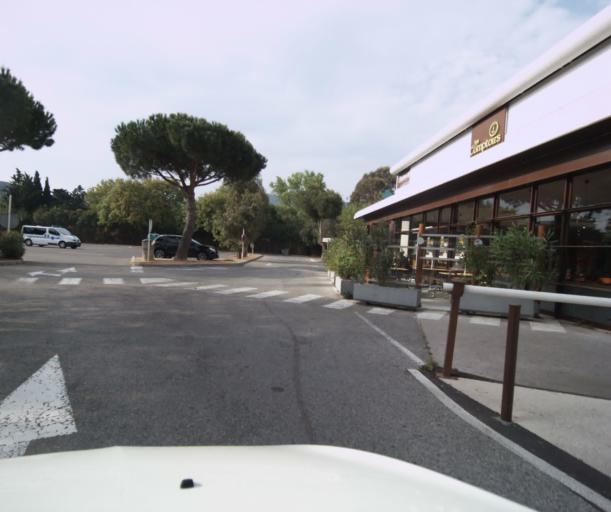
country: FR
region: Provence-Alpes-Cote d'Azur
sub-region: Departement du Var
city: Hyeres
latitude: 43.1151
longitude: 6.1088
